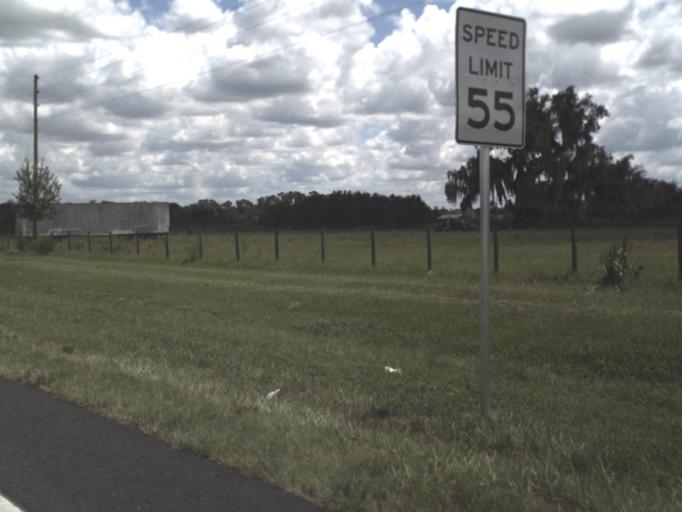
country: US
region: Florida
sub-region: Polk County
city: Wahneta
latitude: 27.9163
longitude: -81.7345
